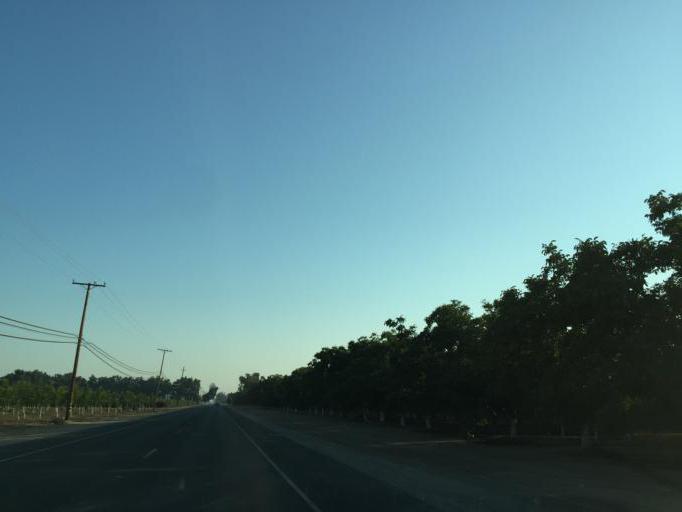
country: US
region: California
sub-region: Tulare County
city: Visalia
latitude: 36.3891
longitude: -119.2966
